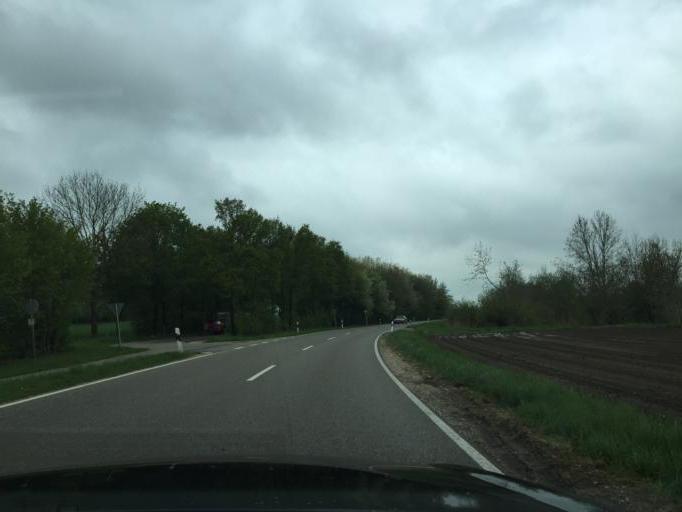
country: DE
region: Bavaria
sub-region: Swabia
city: Buttenwiesen
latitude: 48.5778
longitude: 10.7136
